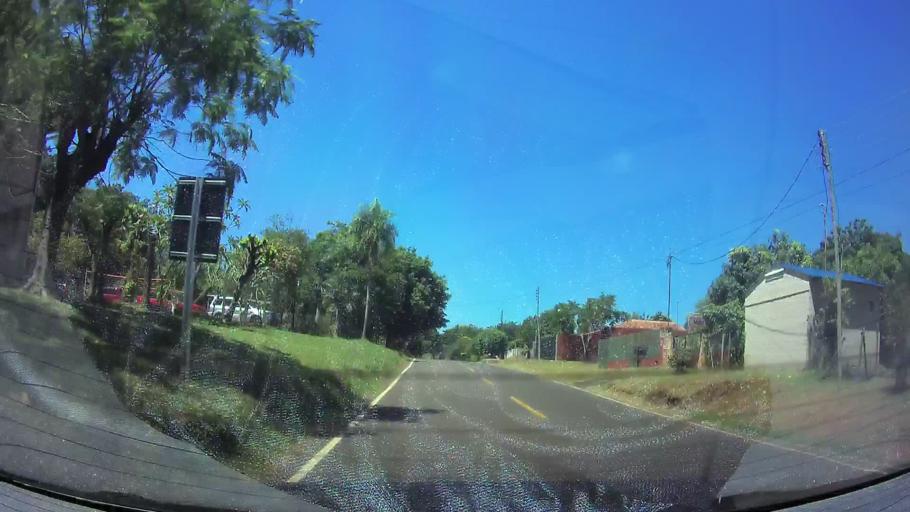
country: PY
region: Central
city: Aregua
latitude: -25.2549
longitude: -57.4452
